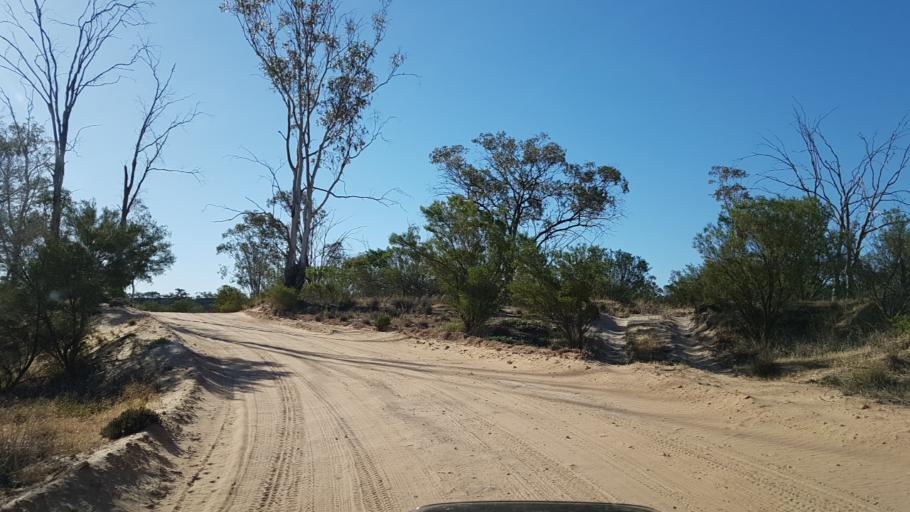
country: AU
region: South Australia
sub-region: Loxton Waikerie
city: Waikerie
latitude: -34.1574
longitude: 140.0250
